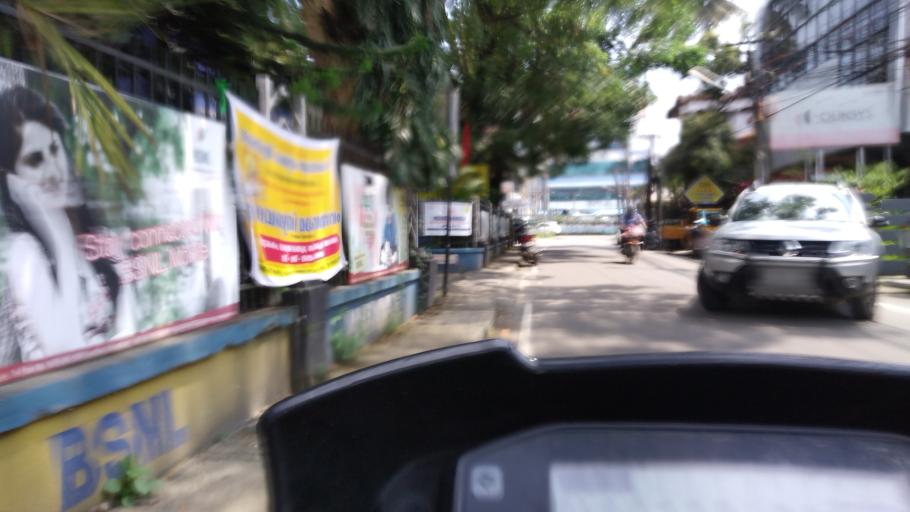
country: IN
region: Kerala
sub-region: Ernakulam
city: Cochin
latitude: 9.9658
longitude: 76.2902
